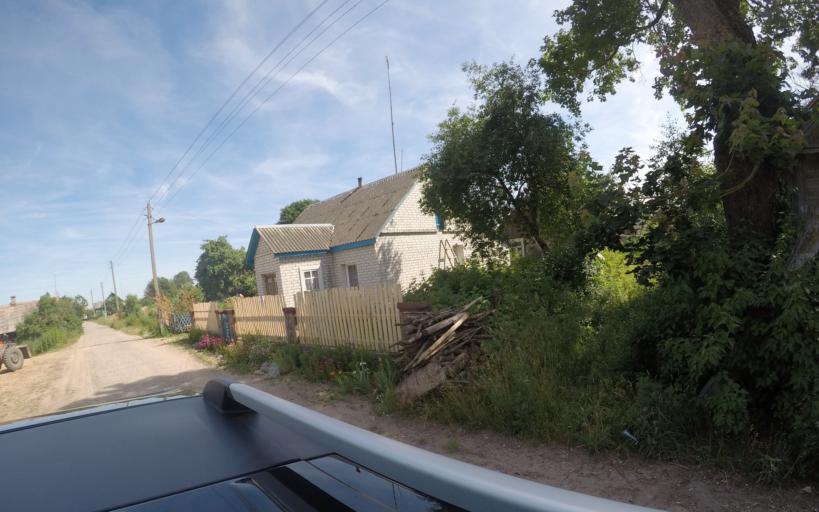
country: BY
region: Grodnenskaya
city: Hal'shany
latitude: 54.2600
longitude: 25.9757
